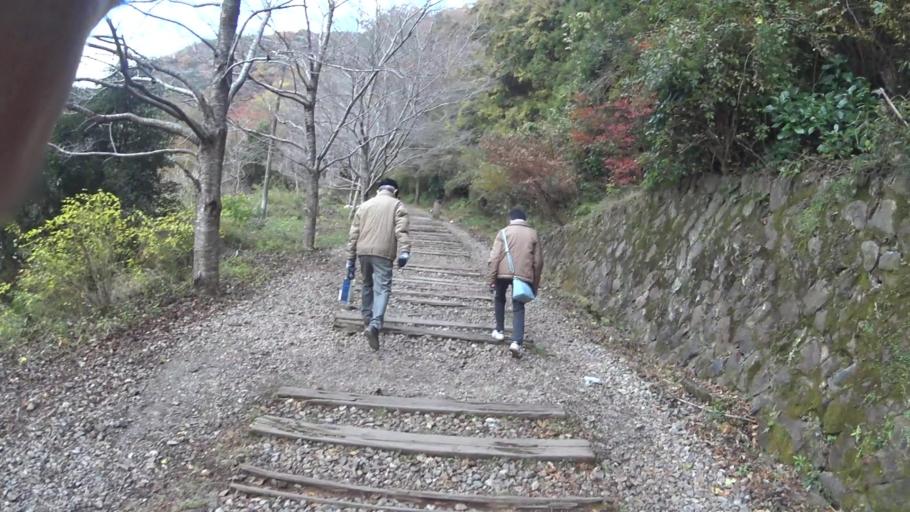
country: JP
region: Hyogo
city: Takarazuka
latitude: 34.8570
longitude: 135.3157
